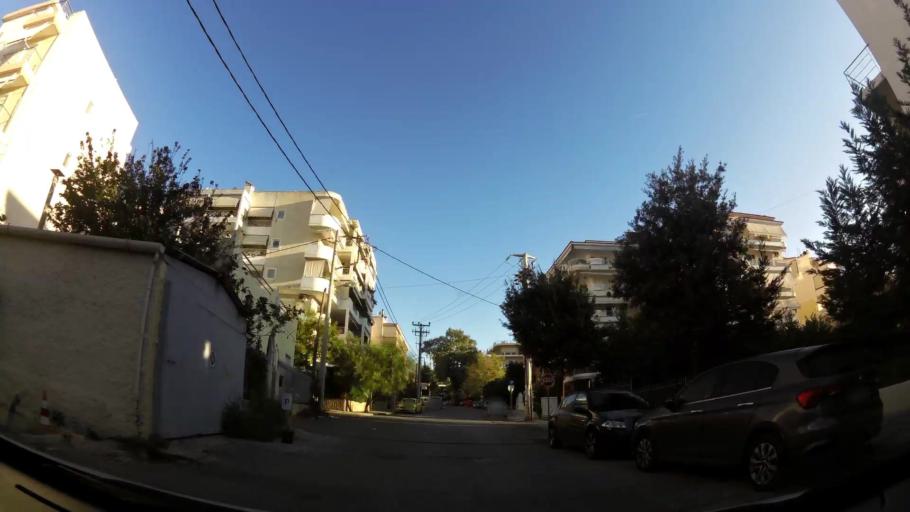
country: GR
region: Attica
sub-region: Nomarchia Athinas
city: Marousi
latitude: 38.0483
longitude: 23.7974
